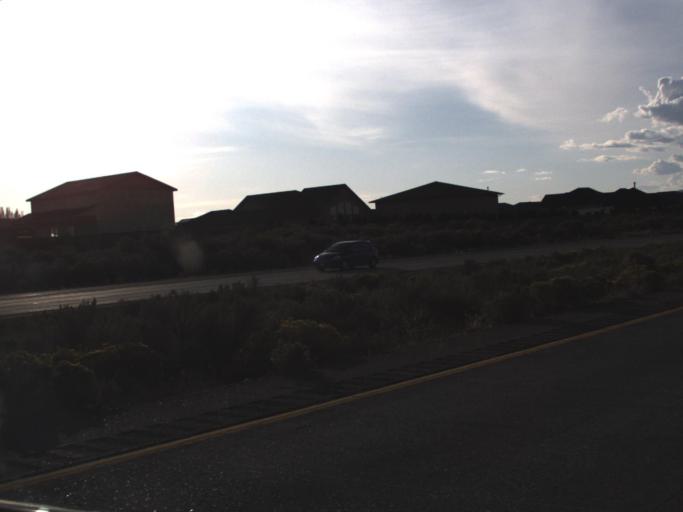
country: US
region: Washington
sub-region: Benton County
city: Richland
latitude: 46.2030
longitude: -119.3313
